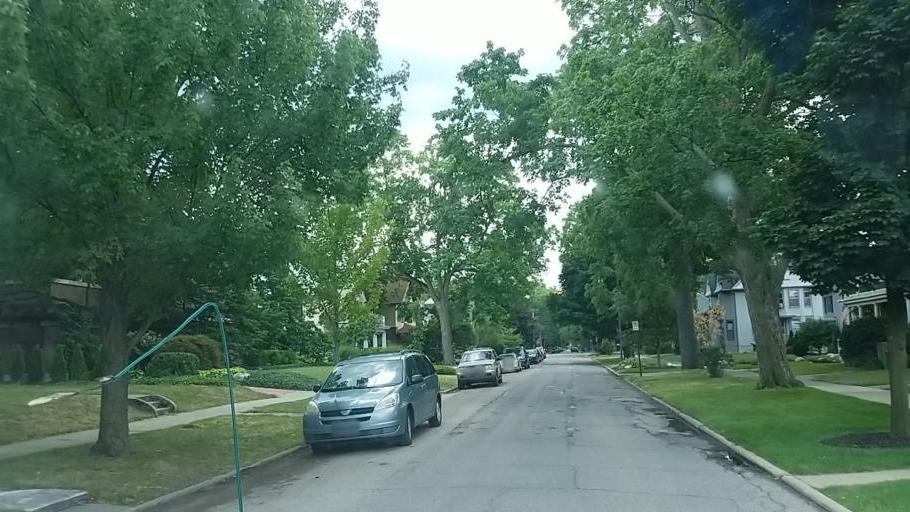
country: US
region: Michigan
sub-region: Kent County
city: Grand Rapids
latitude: 42.9686
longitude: -85.6603
